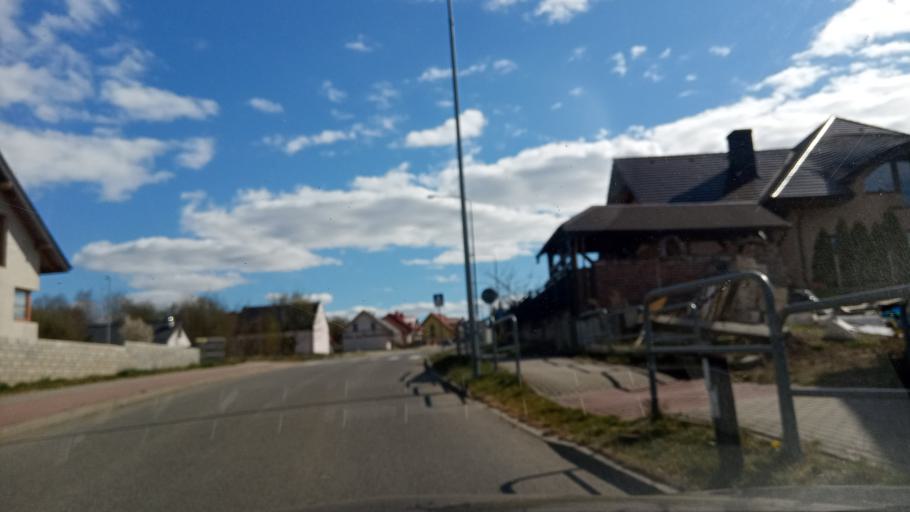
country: PL
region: West Pomeranian Voivodeship
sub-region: Powiat szczecinecki
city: Szczecinek
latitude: 53.7147
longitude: 16.7320
